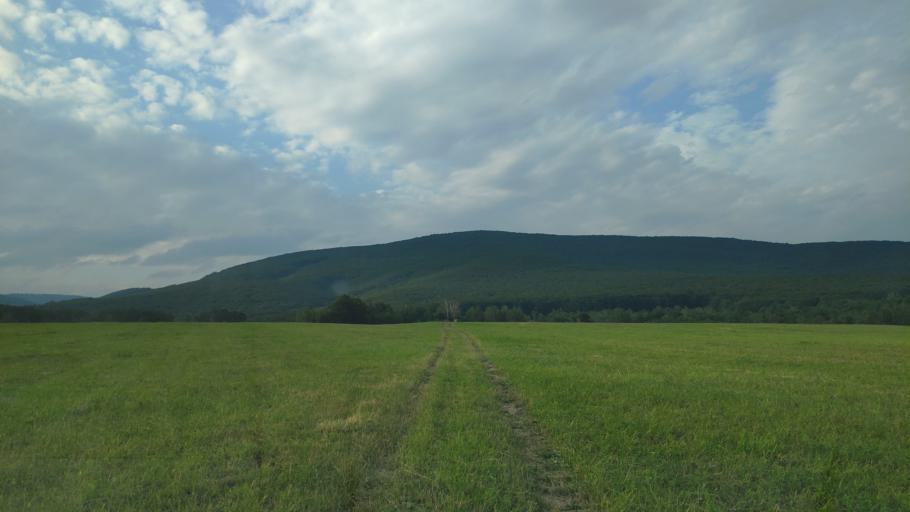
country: SK
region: Kosicky
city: Moldava nad Bodvou
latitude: 48.7127
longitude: 20.9940
